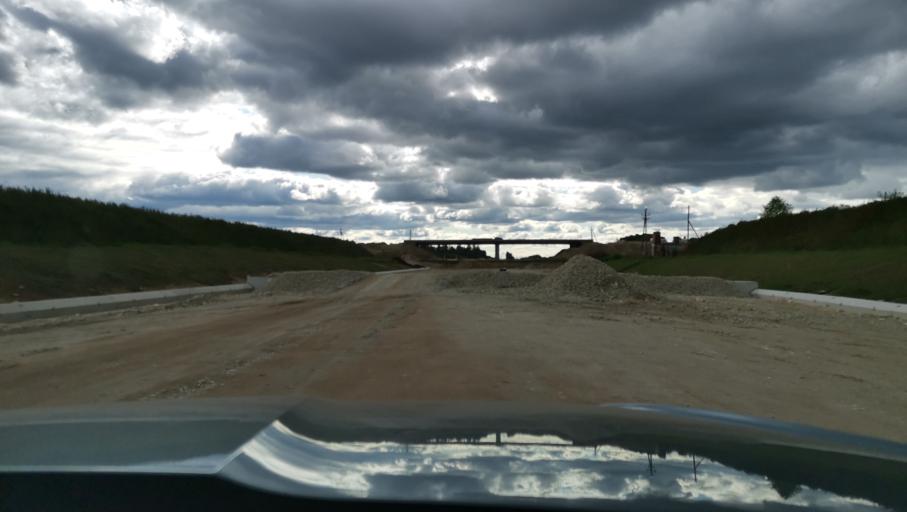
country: EE
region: Harju
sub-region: Nissi vald
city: Riisipere
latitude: 59.1298
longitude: 24.4797
